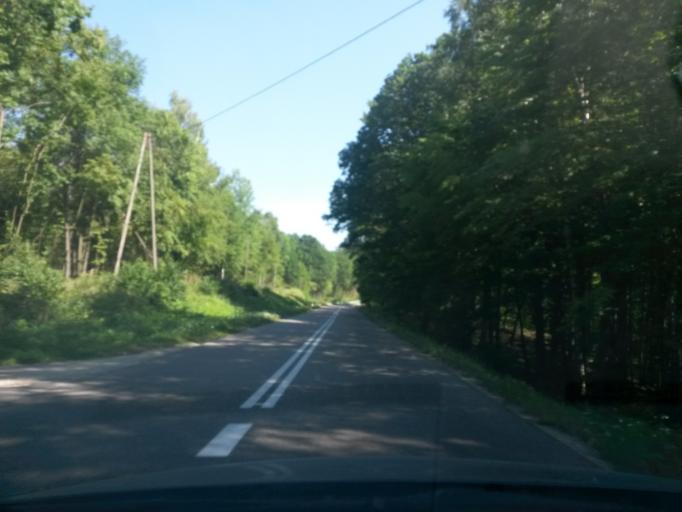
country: PL
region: Kujawsko-Pomorskie
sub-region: Powiat brodnicki
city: Gorzno
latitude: 53.2486
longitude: 19.7077
